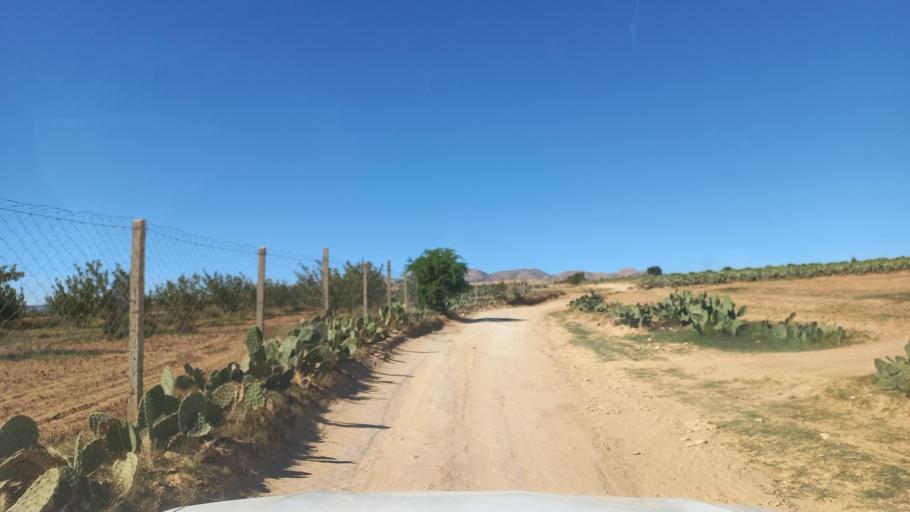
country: TN
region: Al Qasrayn
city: Sbiba
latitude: 35.3727
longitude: 9.0934
